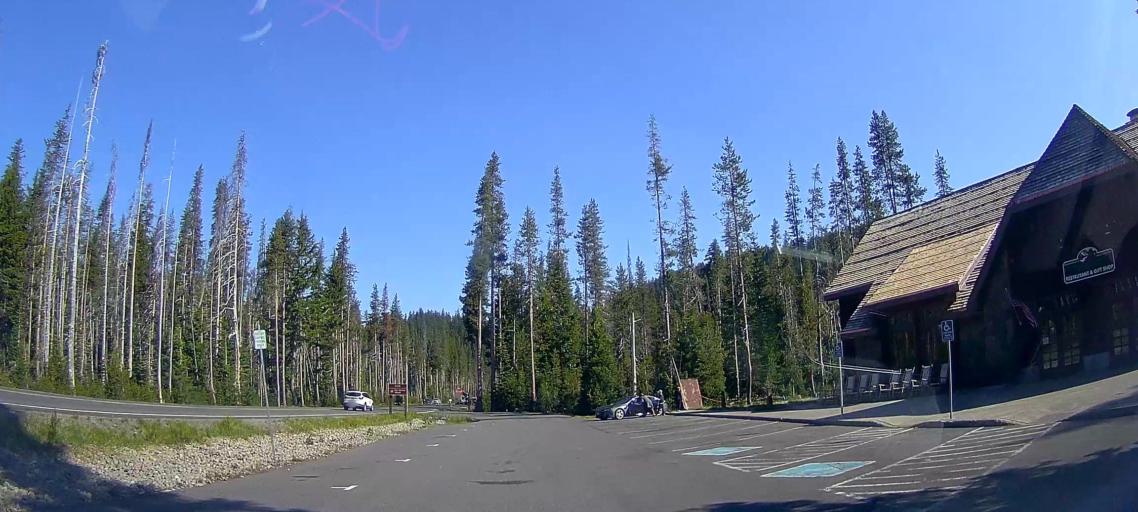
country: US
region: Oregon
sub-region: Jackson County
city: Shady Cove
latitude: 42.8671
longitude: -122.1684
